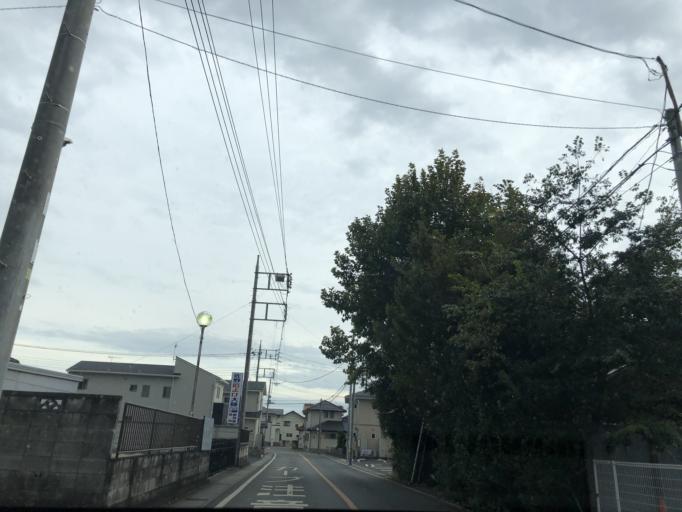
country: JP
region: Tochigi
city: Sano
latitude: 36.3098
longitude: 139.5710
